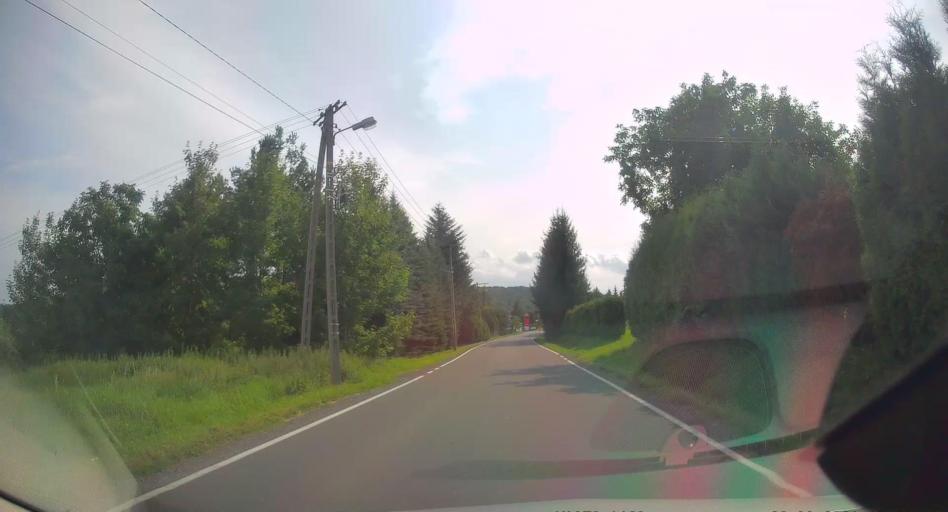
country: PL
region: Lesser Poland Voivodeship
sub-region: Powiat wielicki
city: Pawlikowice
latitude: 49.9457
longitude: 20.0381
